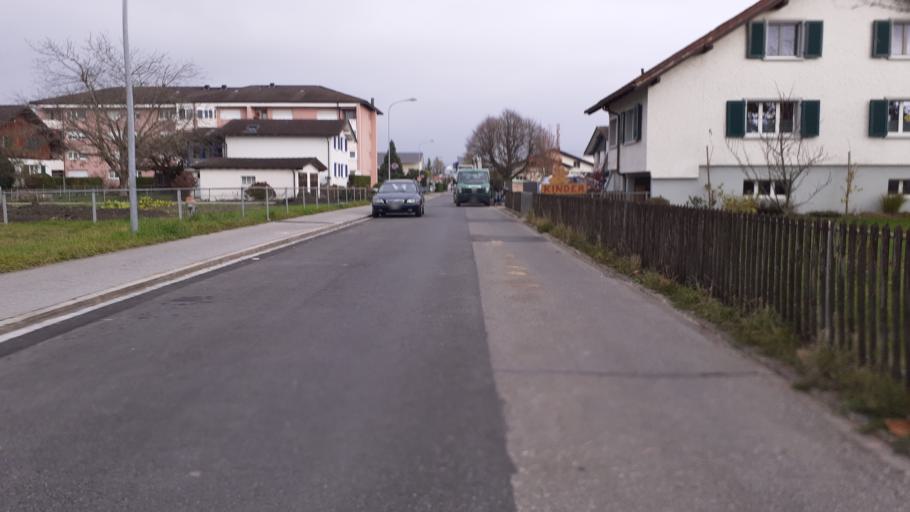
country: CH
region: Saint Gallen
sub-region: Wahlkreis Rheintal
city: Oberriet
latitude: 47.3166
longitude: 9.5677
